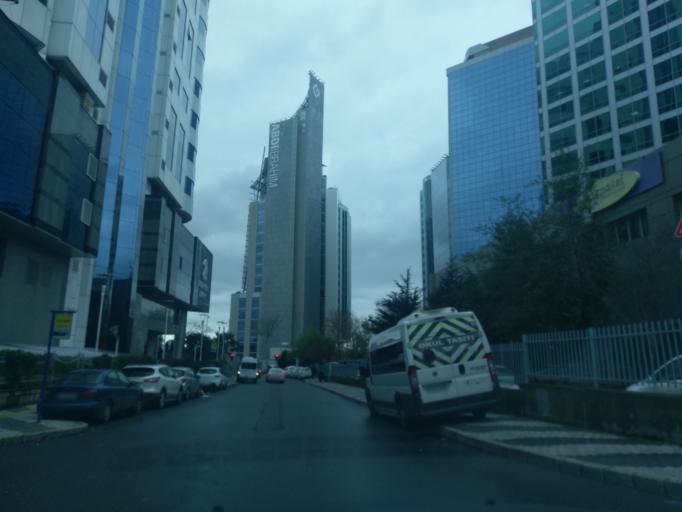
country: TR
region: Istanbul
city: Sisli
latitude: 41.1091
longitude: 29.0166
